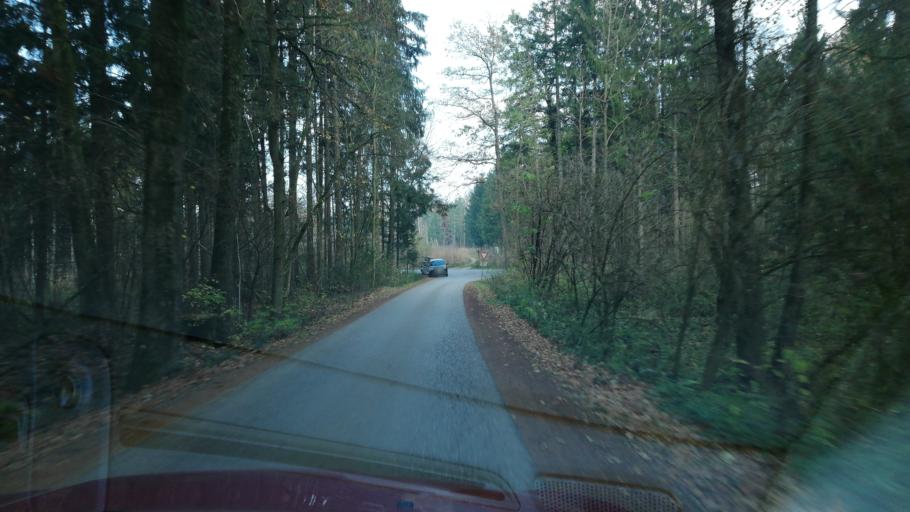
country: AT
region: Upper Austria
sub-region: Politischer Bezirk Kirchdorf an der Krems
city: Kremsmunster
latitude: 48.1072
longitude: 14.1726
